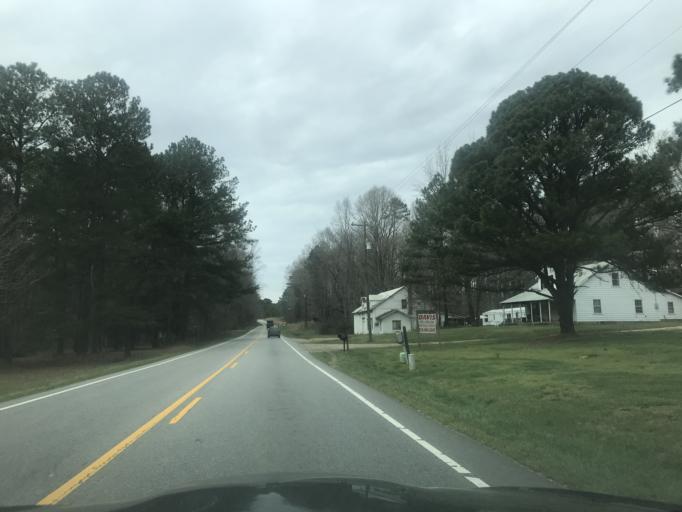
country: US
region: North Carolina
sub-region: Franklin County
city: Franklinton
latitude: 36.1103
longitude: -78.4771
